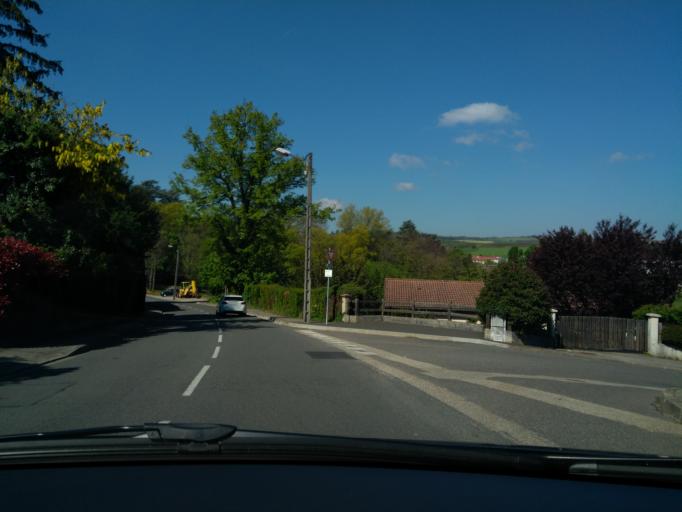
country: FR
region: Rhone-Alpes
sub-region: Departement de la Loire
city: Villars
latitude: 45.4666
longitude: 4.3512
